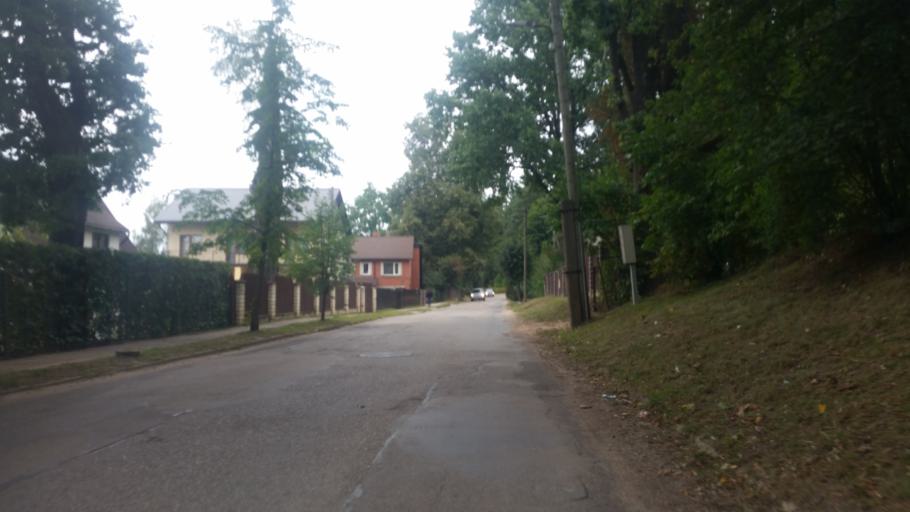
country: LV
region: Ogre
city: Ogre
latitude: 56.8108
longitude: 24.6172
